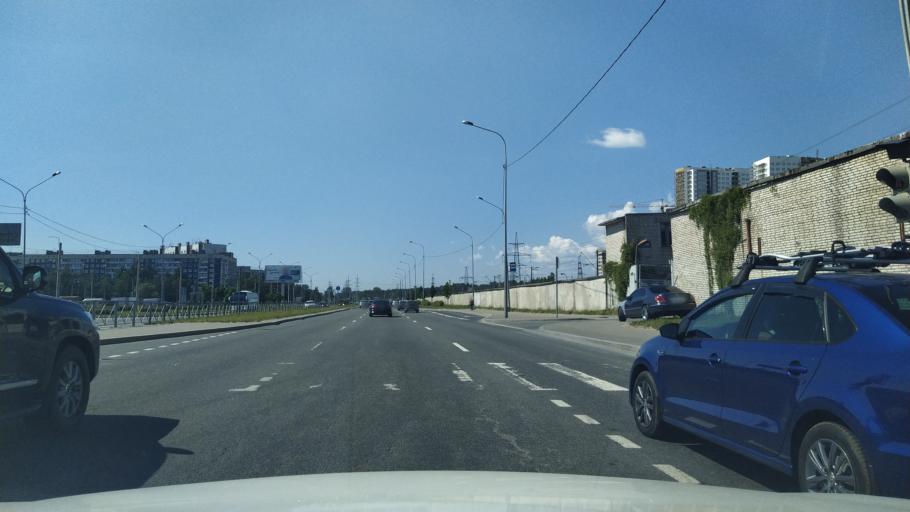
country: RU
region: St.-Petersburg
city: Ozerki
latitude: 60.0651
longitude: 30.3206
